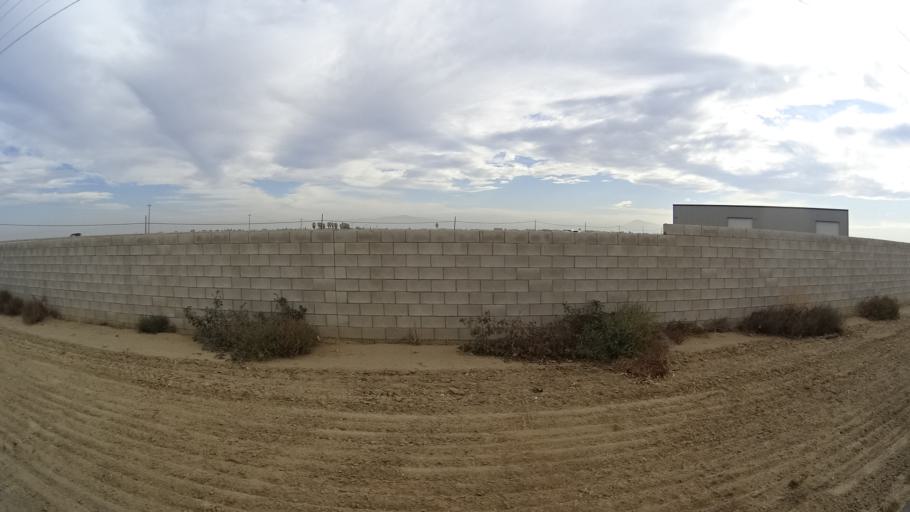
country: US
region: California
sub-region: Kern County
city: Rosedale
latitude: 35.4113
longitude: -119.1633
